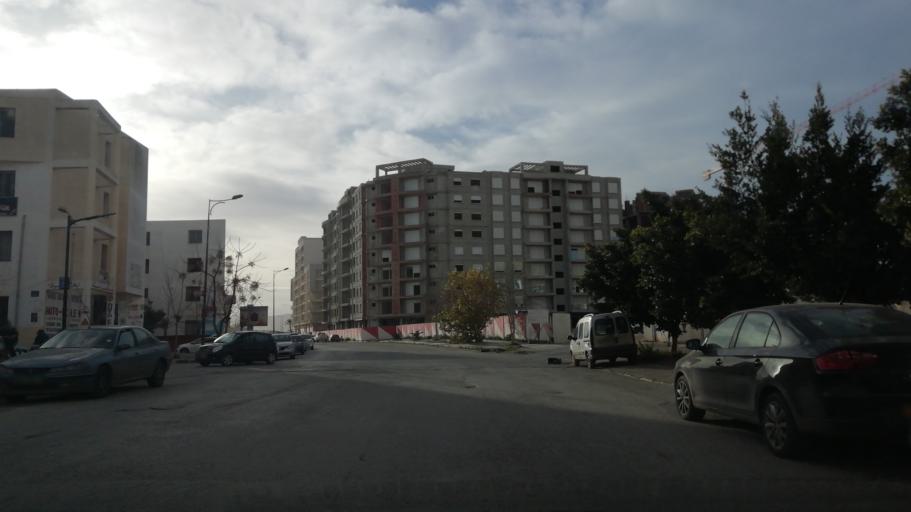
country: DZ
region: Oran
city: Bir el Djir
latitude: 35.7246
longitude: -0.5901
